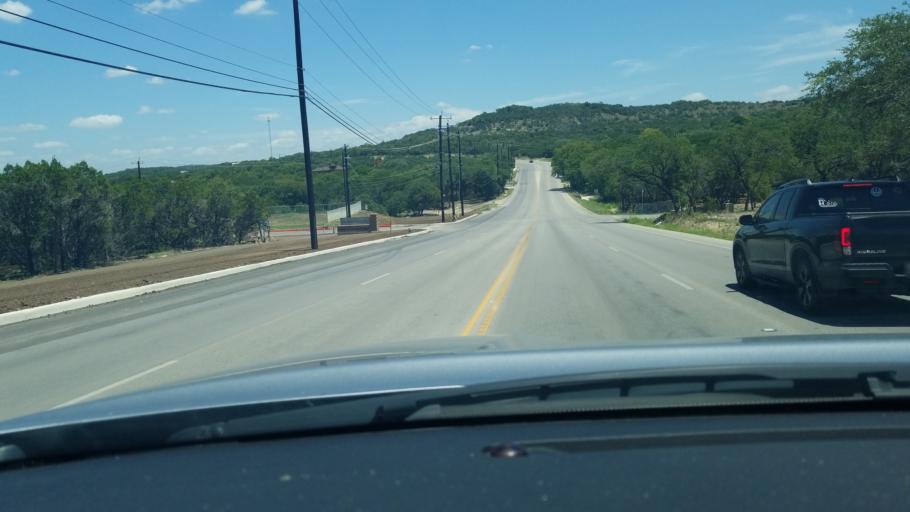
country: US
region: Texas
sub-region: Bexar County
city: Timberwood Park
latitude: 29.7146
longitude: -98.4704
